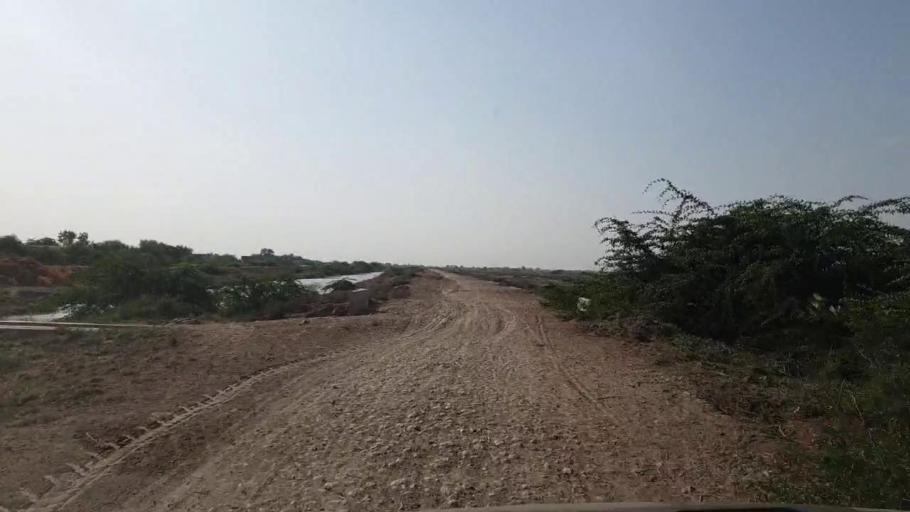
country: PK
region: Sindh
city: Kadhan
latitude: 24.6375
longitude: 69.0723
